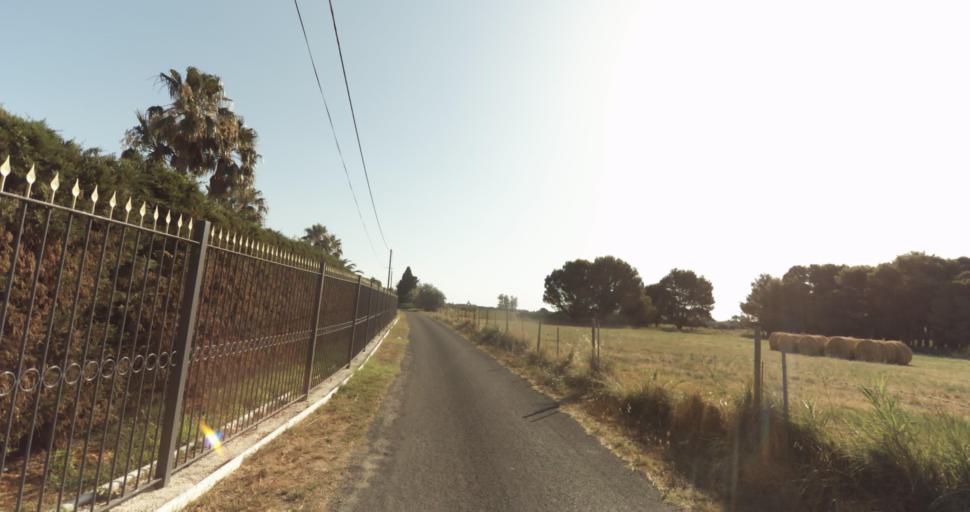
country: FR
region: Languedoc-Roussillon
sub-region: Departement des Pyrenees-Orientales
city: Alenya
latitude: 42.6369
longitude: 3.0057
